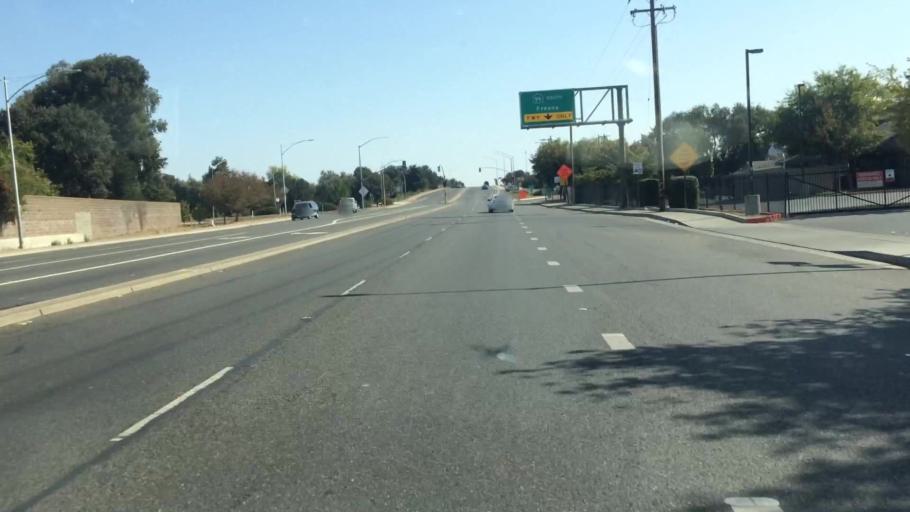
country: US
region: California
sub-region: Sacramento County
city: Parkway
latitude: 38.5103
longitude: -121.4640
